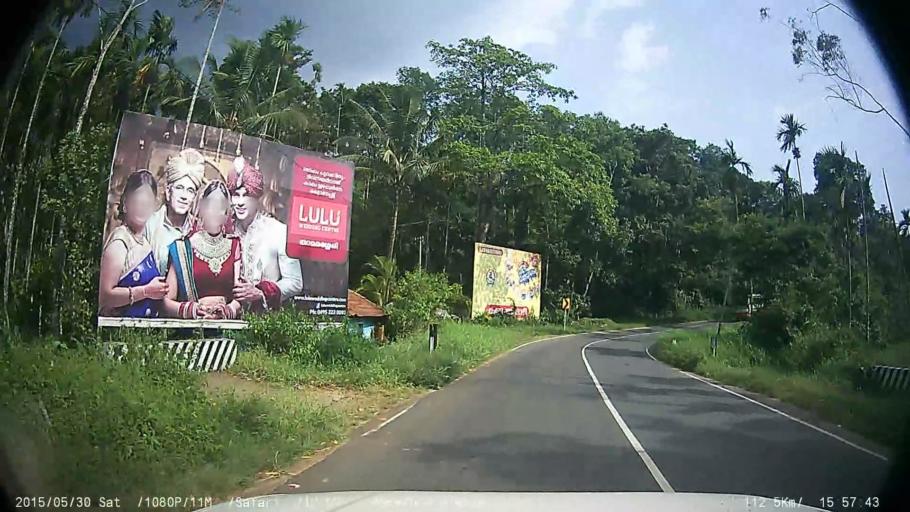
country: IN
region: Kerala
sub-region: Wayanad
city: Kalpetta
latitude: 11.6537
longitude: 76.0887
